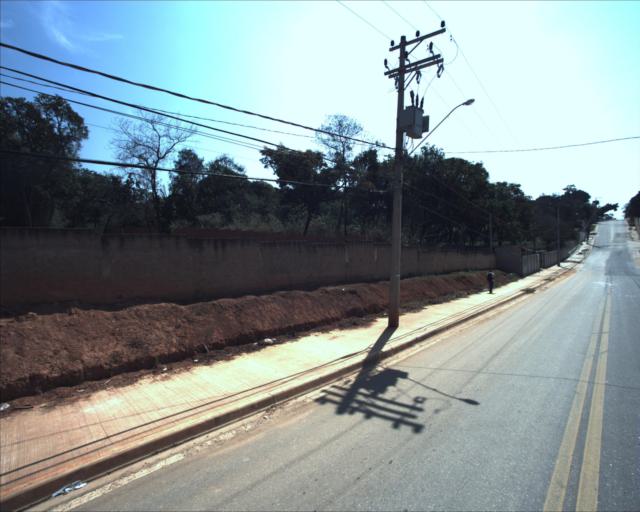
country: BR
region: Sao Paulo
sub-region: Sorocaba
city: Sorocaba
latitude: -23.4488
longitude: -47.4972
